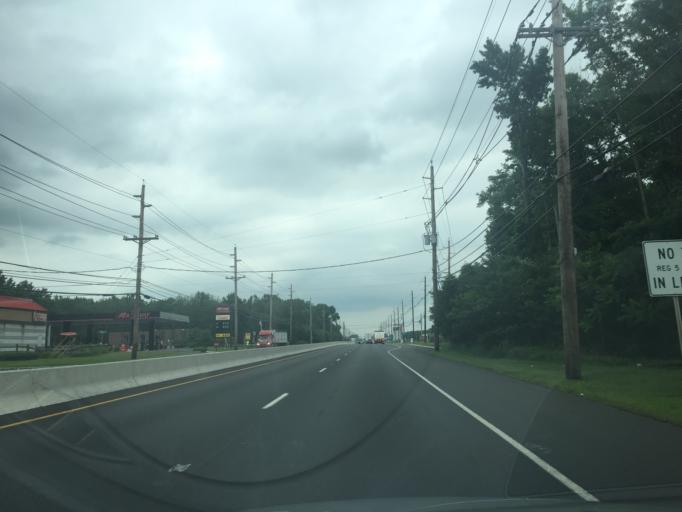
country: US
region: New Jersey
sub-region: Middlesex County
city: Kendall Park
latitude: 40.4343
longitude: -74.5127
